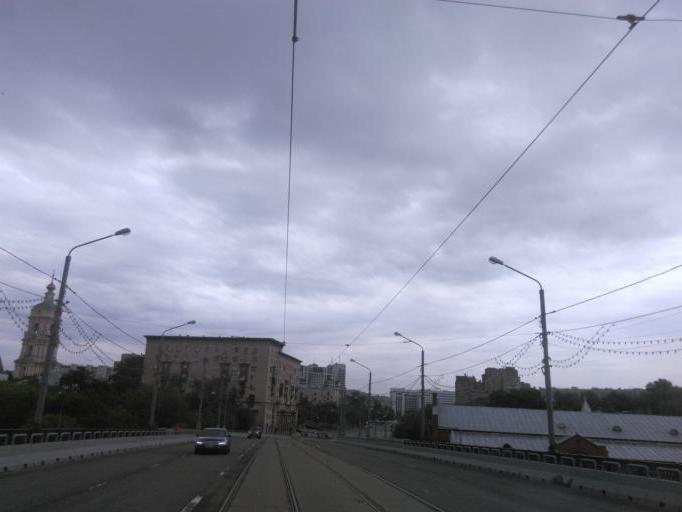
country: RU
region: Moscow
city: Taganskiy
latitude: 55.7290
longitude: 37.6543
